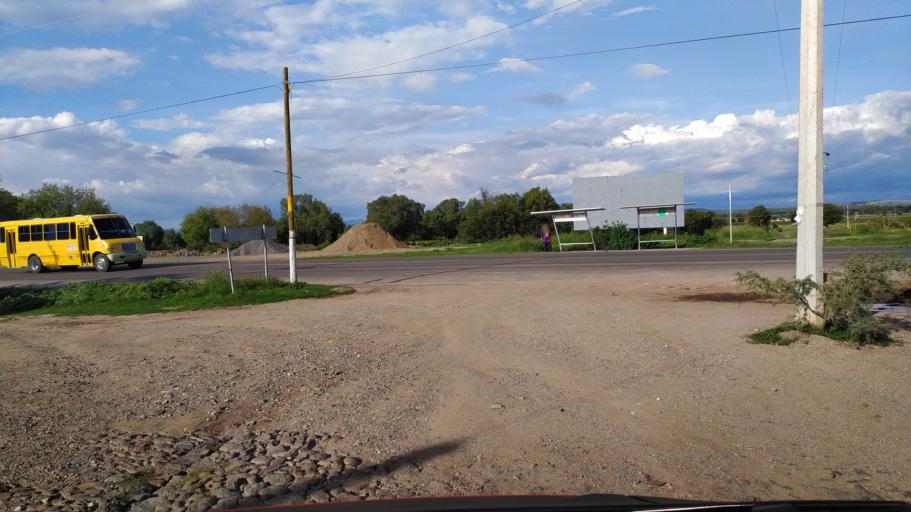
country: MX
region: Guanajuato
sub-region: San Francisco del Rincon
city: San Ignacio de Hidalgo
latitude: 20.9273
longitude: -101.9178
